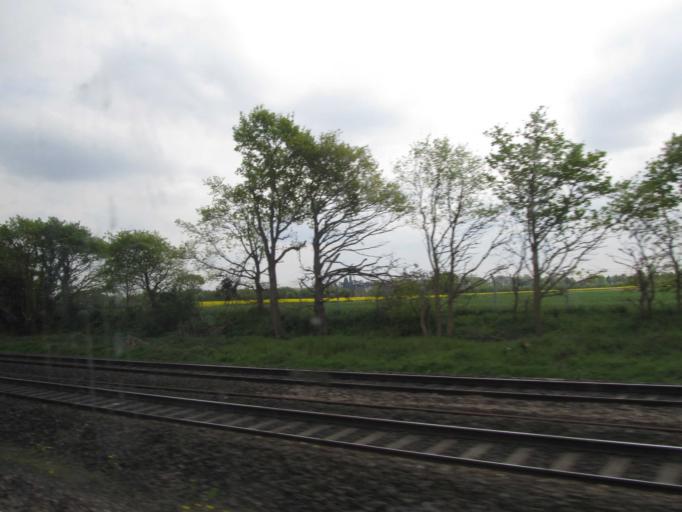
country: GB
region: England
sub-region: Buckinghamshire
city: Iver
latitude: 51.5078
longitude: -0.5201
